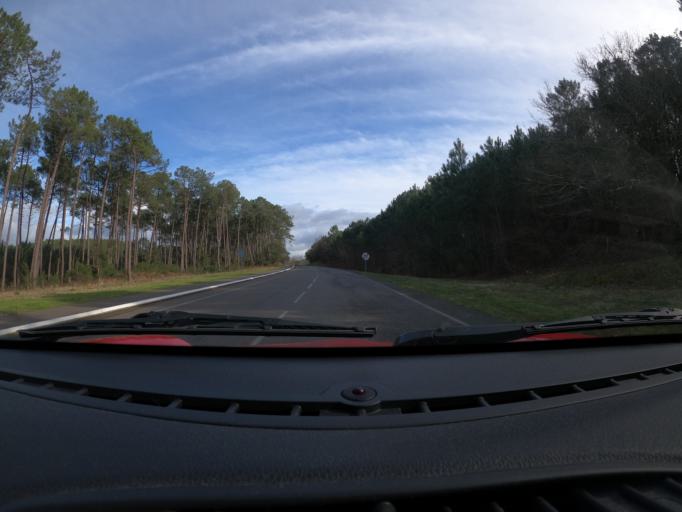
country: FR
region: Aquitaine
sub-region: Departement des Landes
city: Labenne
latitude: 43.5882
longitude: -1.4170
